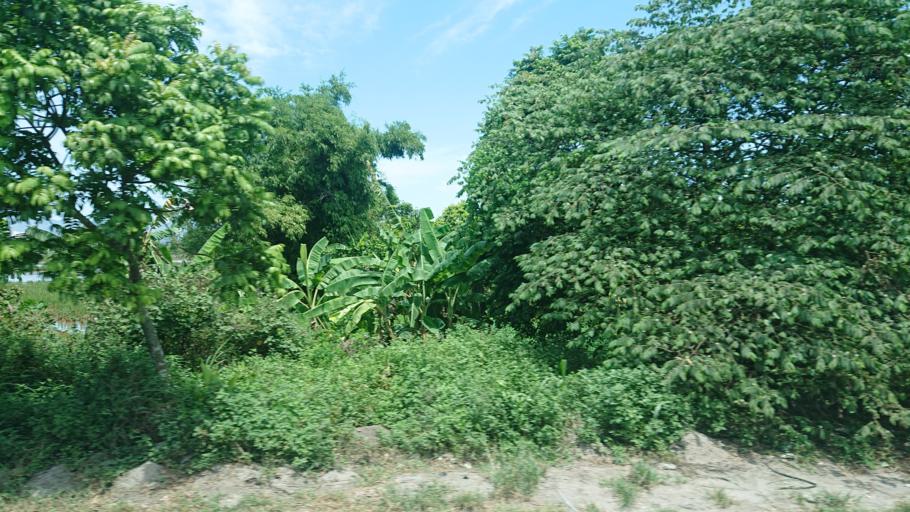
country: VN
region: Ha Nam
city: Thanh Pho Phu Ly
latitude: 20.5190
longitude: 105.9437
